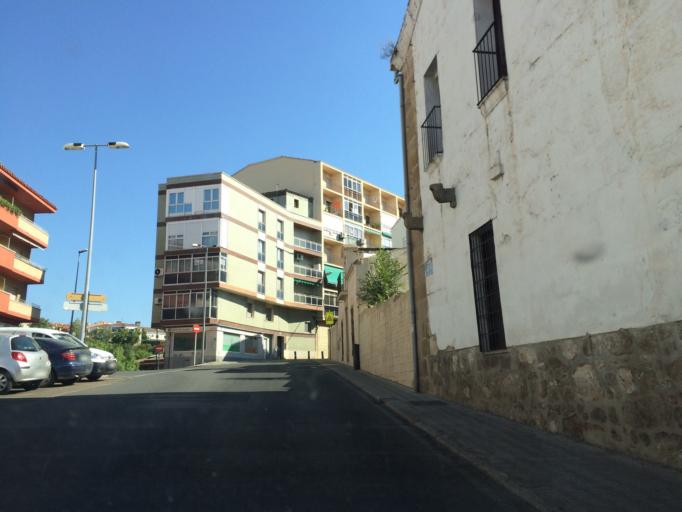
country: ES
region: Extremadura
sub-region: Provincia de Caceres
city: Plasencia
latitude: 40.0308
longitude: -6.0923
